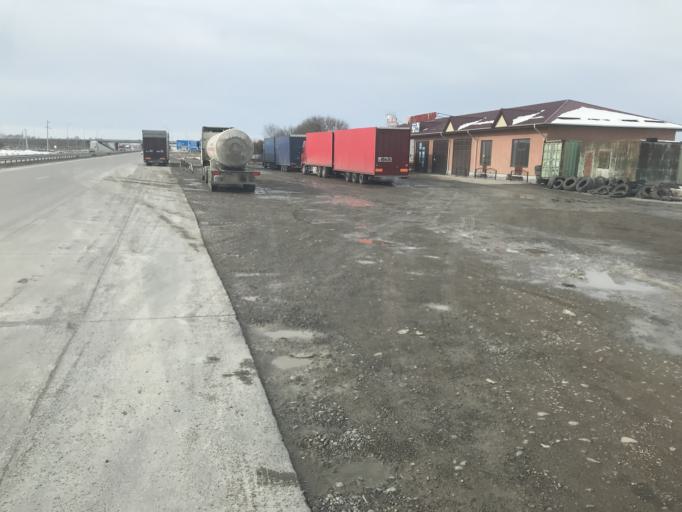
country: KZ
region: Ongtustik Qazaqstan
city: Aksu
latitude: 42.4746
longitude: 69.8201
